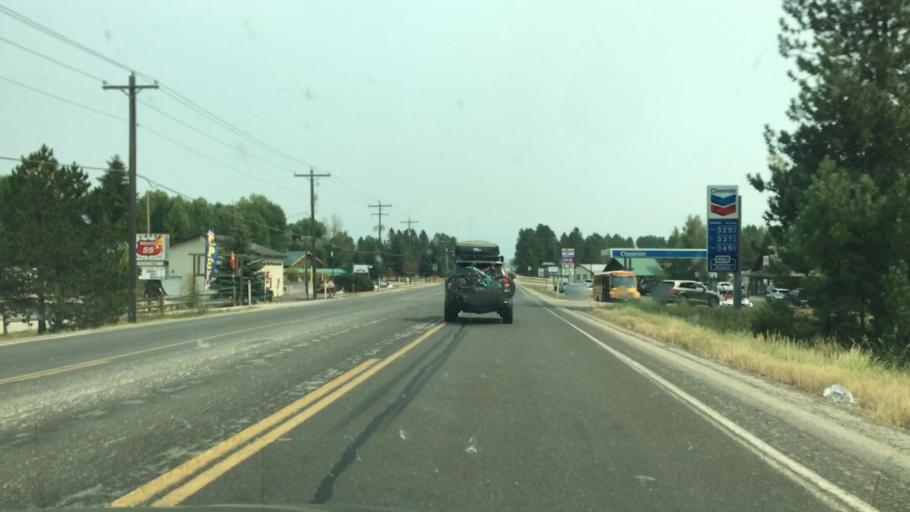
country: US
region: Idaho
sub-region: Valley County
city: Cascade
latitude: 44.5058
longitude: -116.0304
